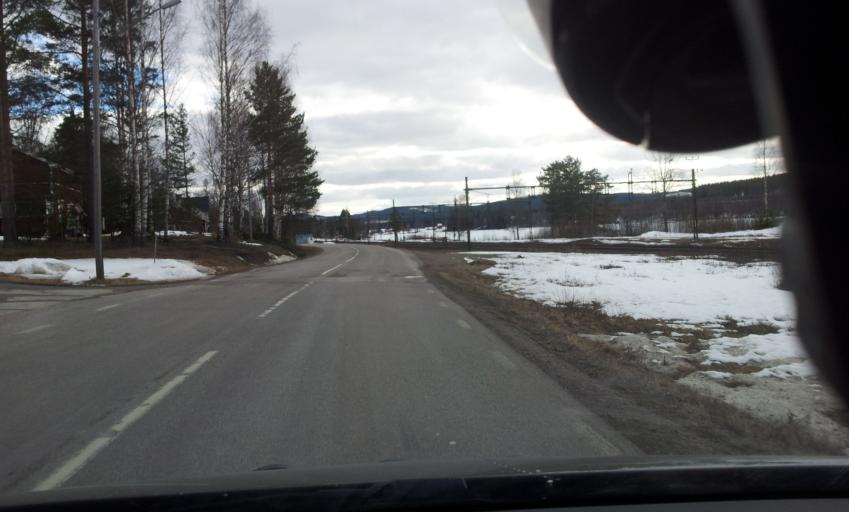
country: SE
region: Vaesternorrland
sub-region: Ange Kommun
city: Ange
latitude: 62.1625
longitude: 15.6777
